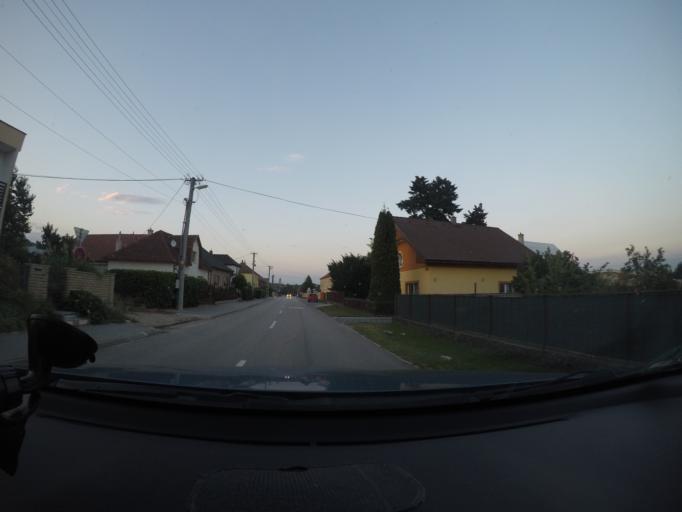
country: SK
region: Trenciansky
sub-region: Okres Nove Mesto nad Vahom
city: Nove Mesto nad Vahom
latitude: 48.8472
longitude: 17.9164
